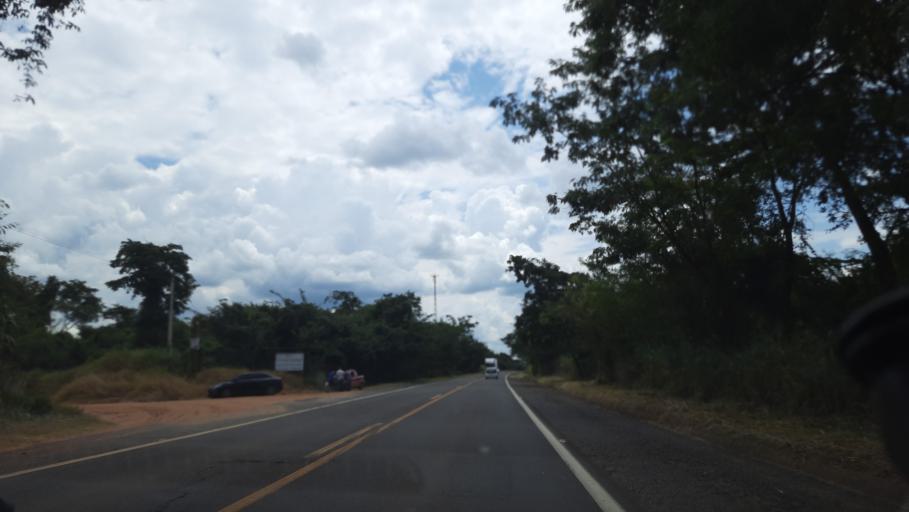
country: BR
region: Sao Paulo
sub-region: Mococa
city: Mococa
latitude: -21.4918
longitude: -47.0746
